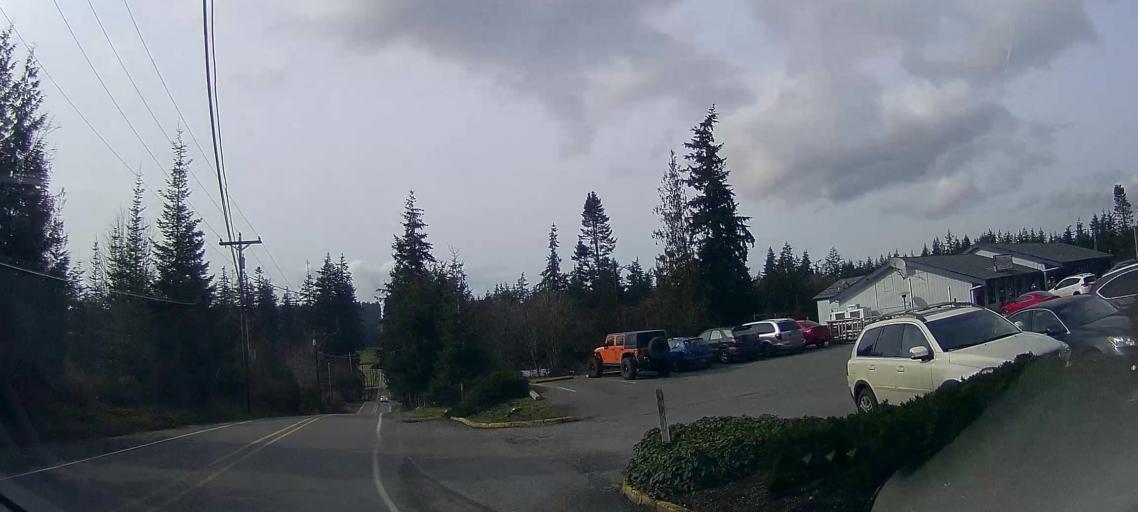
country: US
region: Washington
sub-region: Island County
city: Camano
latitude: 48.1380
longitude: -122.4679
